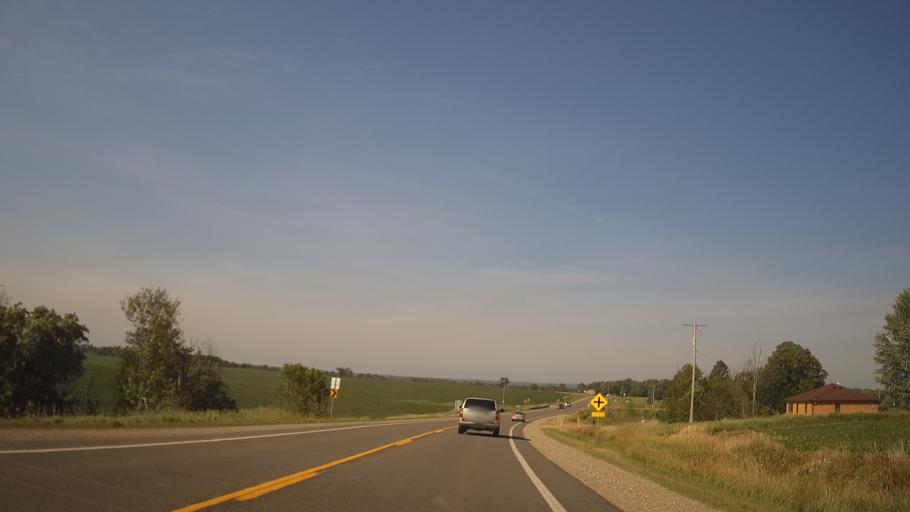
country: US
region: Michigan
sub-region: Ogemaw County
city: West Branch
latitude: 44.3614
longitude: -84.1242
